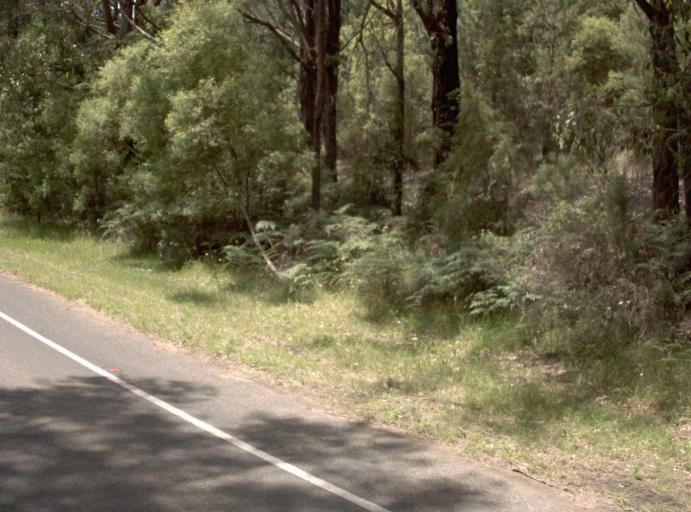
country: AU
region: Victoria
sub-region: Latrobe
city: Traralgon
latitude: -38.3582
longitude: 146.7487
